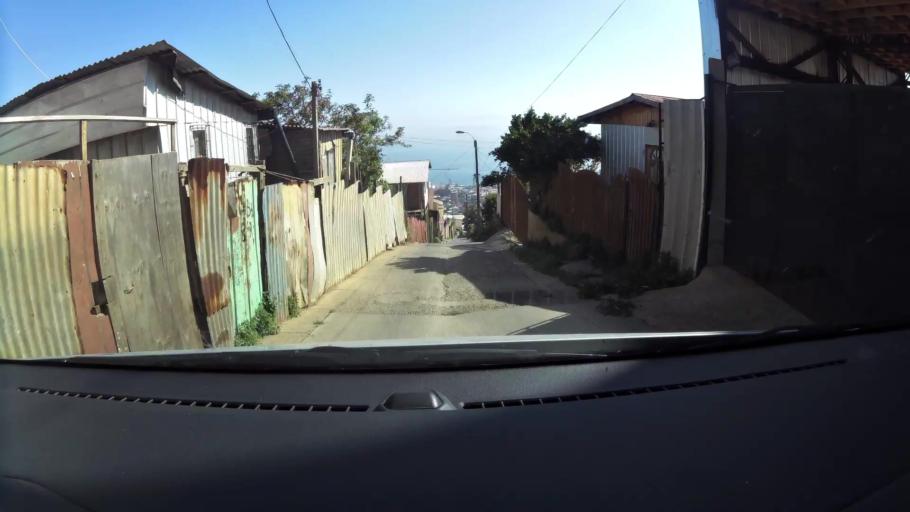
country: CL
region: Valparaiso
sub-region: Provincia de Valparaiso
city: Valparaiso
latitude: -33.0525
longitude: -71.6390
